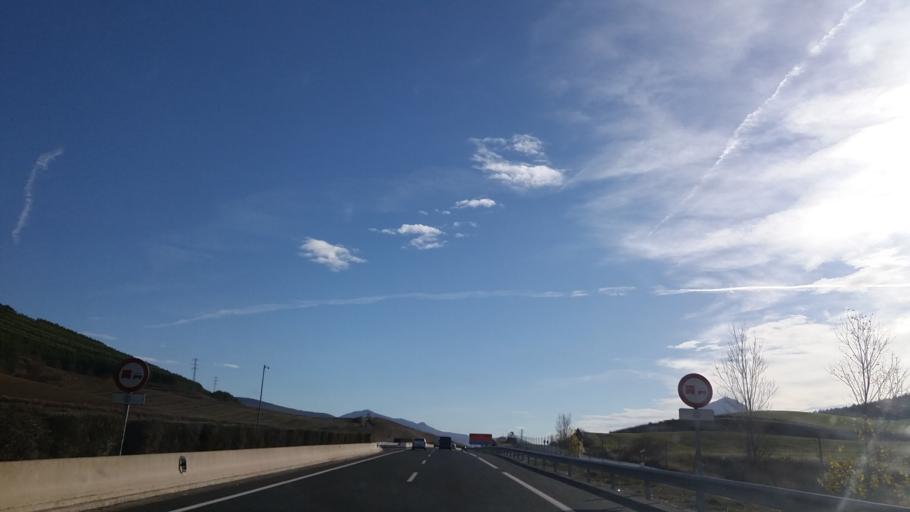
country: ES
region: Navarre
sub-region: Provincia de Navarra
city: Beriain
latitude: 42.7538
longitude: -1.6143
